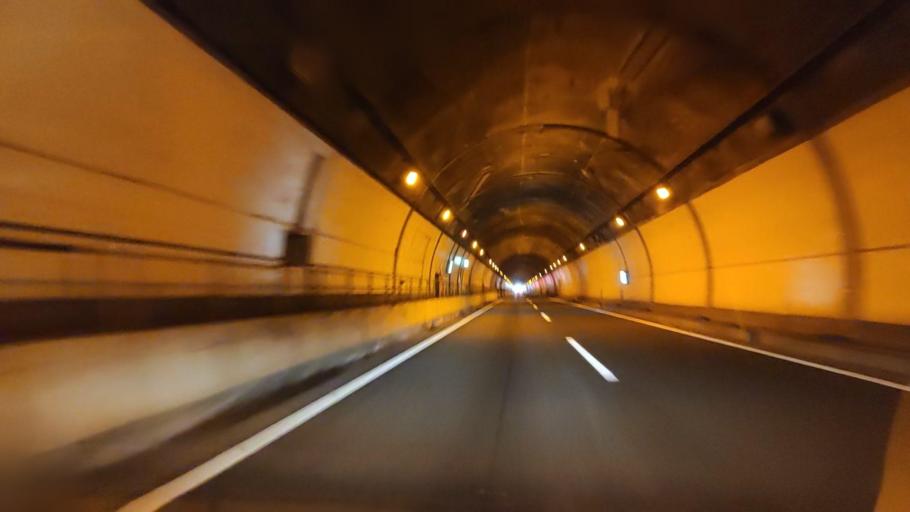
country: JP
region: Akita
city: Hanawa
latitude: 40.0100
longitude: 140.9886
